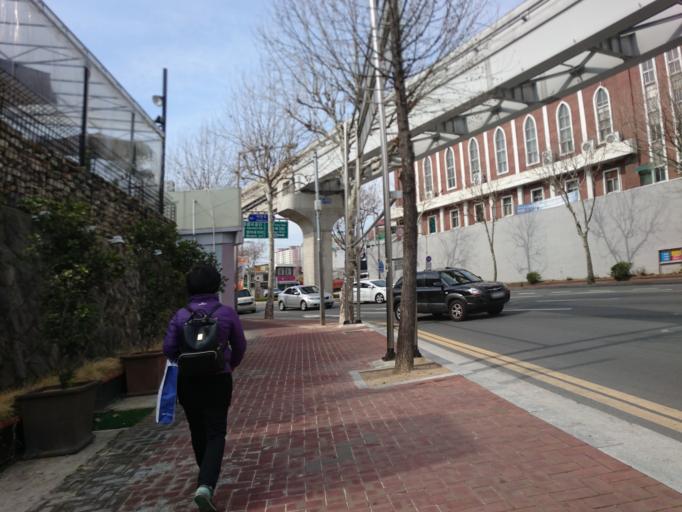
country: KR
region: Daegu
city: Daegu
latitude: 35.8557
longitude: 128.5979
